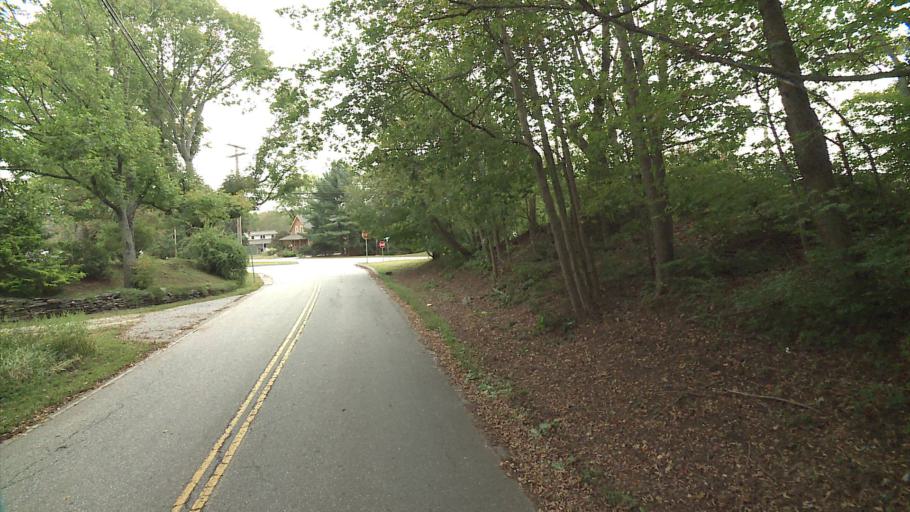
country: US
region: Connecticut
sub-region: Windham County
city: Wauregan
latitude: 41.7221
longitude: -71.9145
